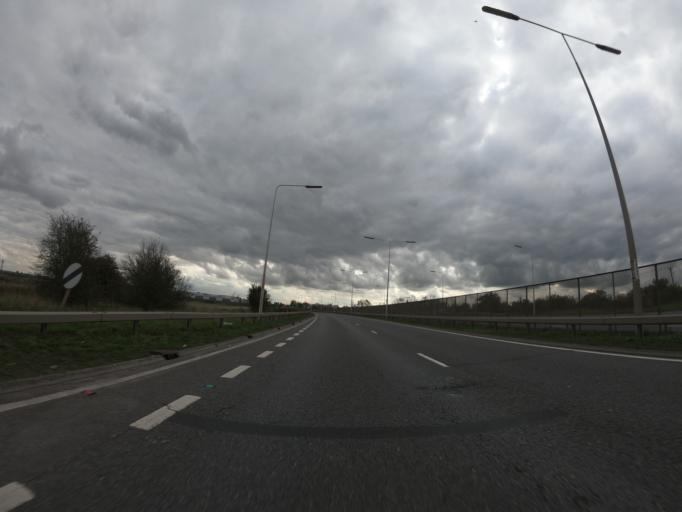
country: GB
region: England
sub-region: Borough of Thurrock
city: Chadwell St Mary
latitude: 51.4757
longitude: 0.3485
